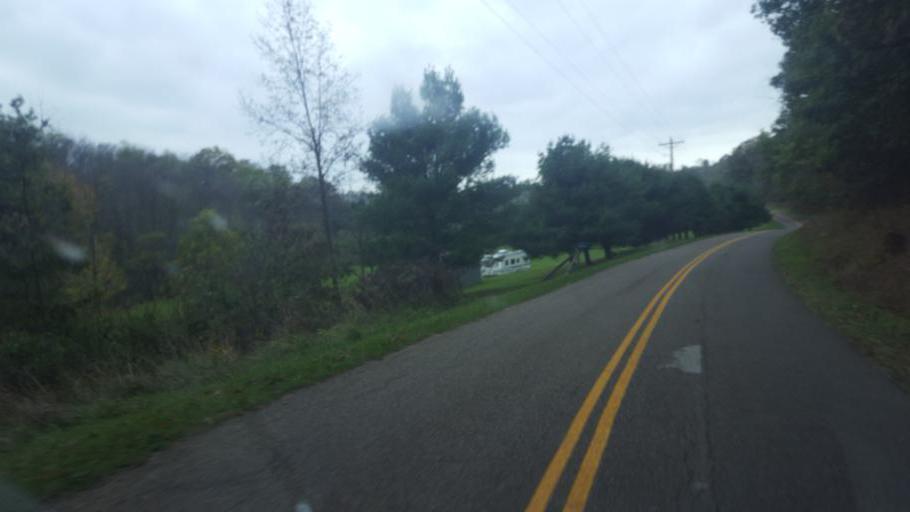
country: US
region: Ohio
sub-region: Carroll County
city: Carrollton
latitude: 40.4812
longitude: -81.0810
